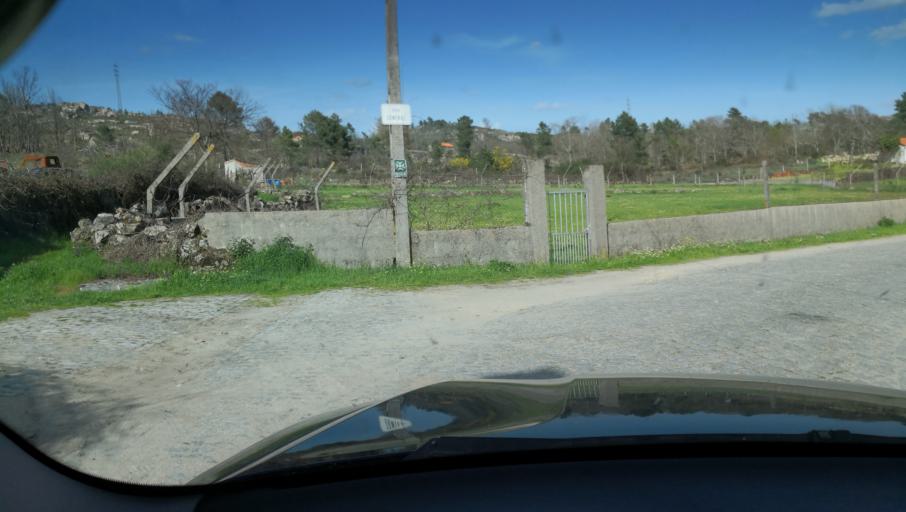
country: PT
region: Vila Real
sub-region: Vila Real
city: Vila Real
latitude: 41.2852
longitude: -7.6644
